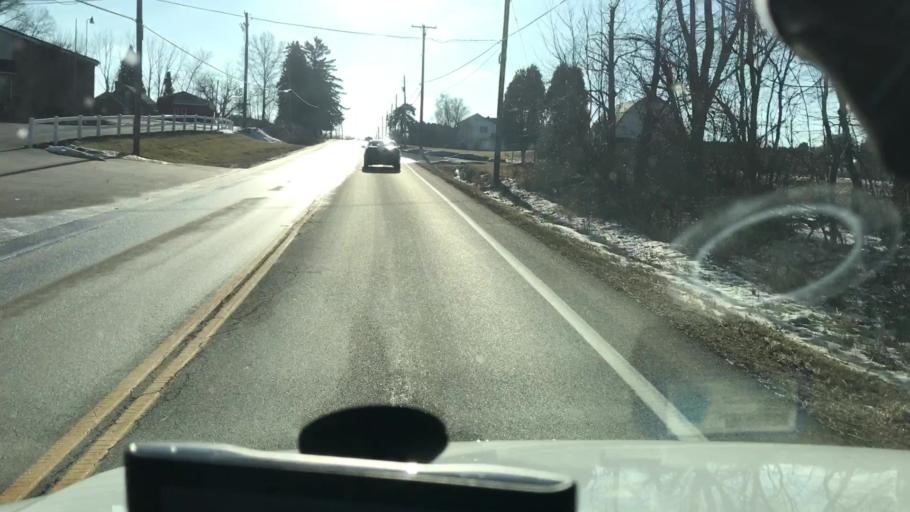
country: US
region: Ohio
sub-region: Mahoning County
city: New Middletown
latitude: 40.9302
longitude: -80.6262
